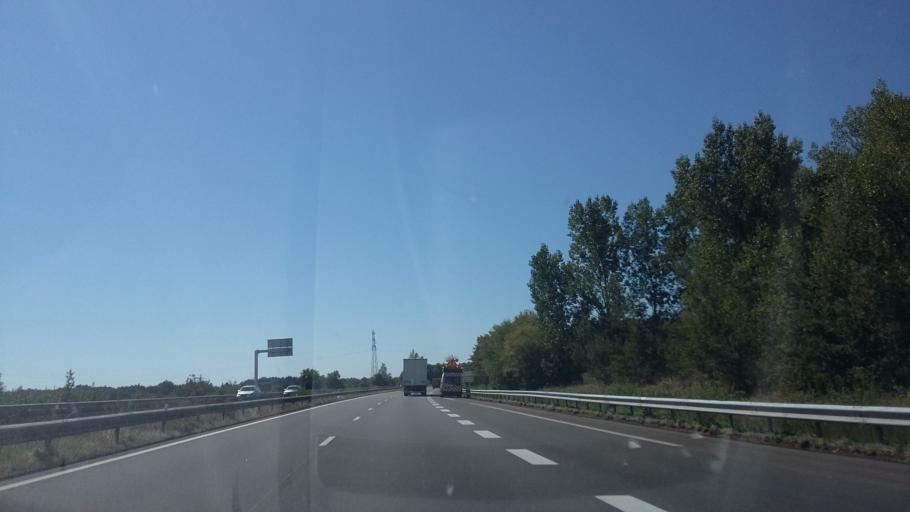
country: FR
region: Rhone-Alpes
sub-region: Departement de la Loire
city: Feurs
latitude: 45.7326
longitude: 4.1827
